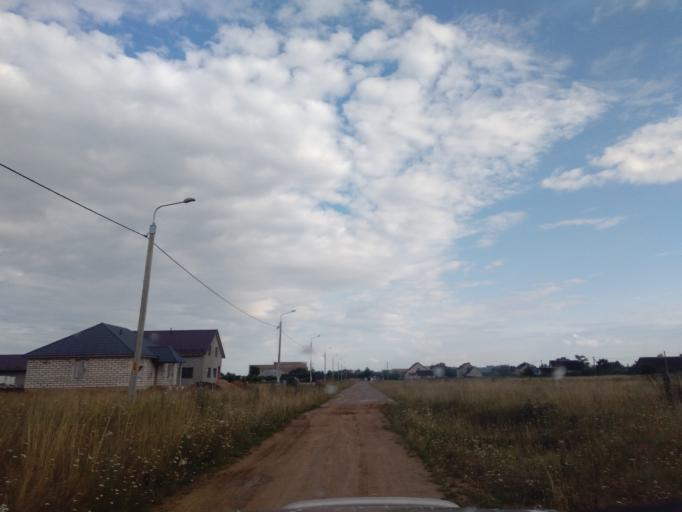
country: BY
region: Minsk
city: Kapyl'
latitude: 53.1635
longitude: 27.0801
